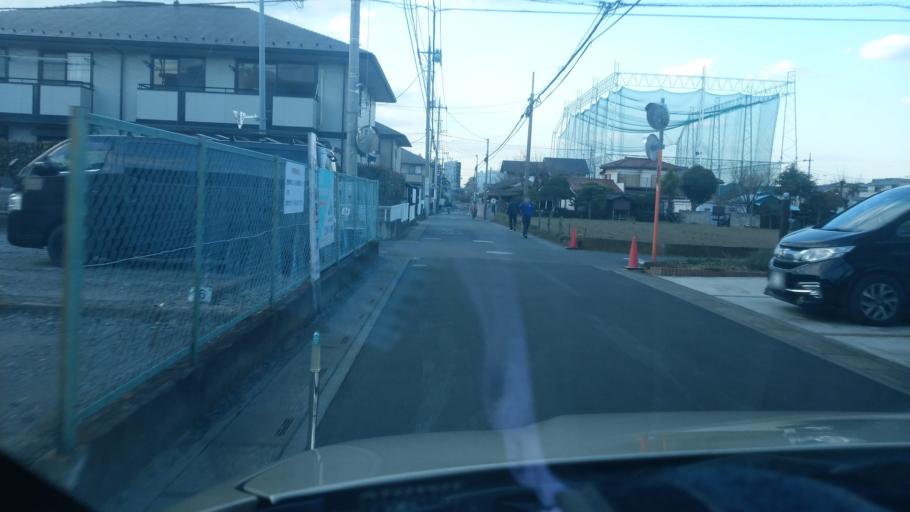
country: JP
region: Saitama
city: Yono
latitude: 35.8943
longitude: 139.6008
